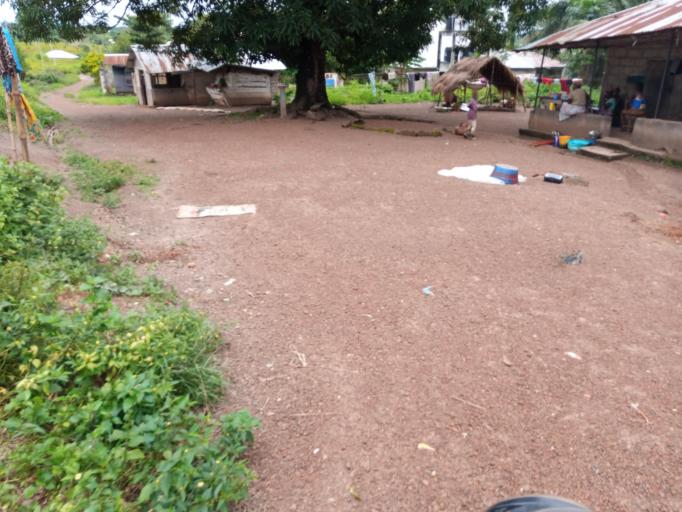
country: SL
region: Southern Province
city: Largo
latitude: 8.2001
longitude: -12.0651
